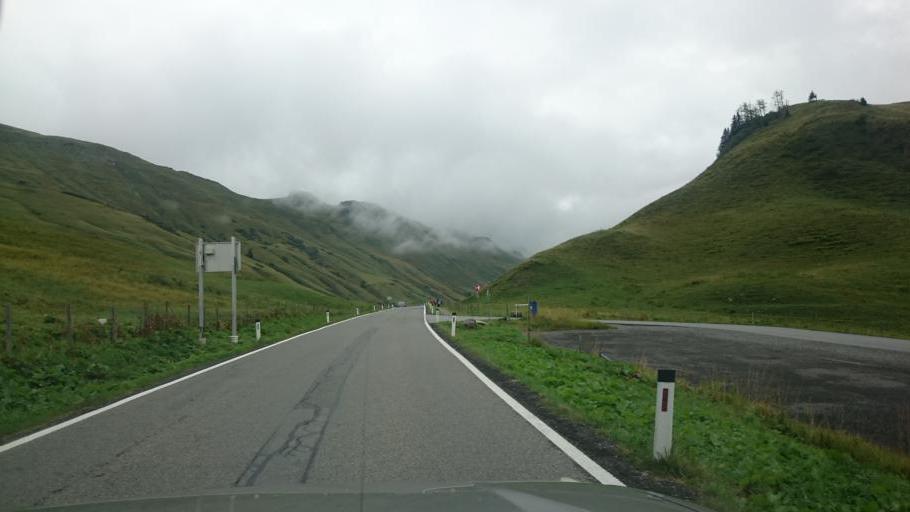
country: AT
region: Vorarlberg
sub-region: Politischer Bezirk Bregenz
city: Schroecken
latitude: 47.2691
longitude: 10.1290
